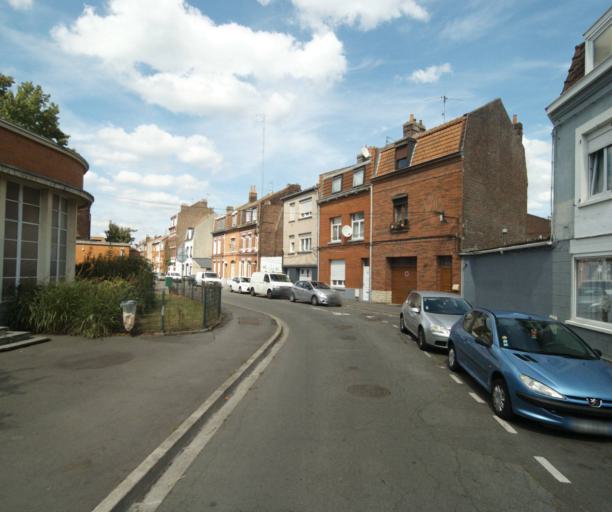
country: FR
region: Nord-Pas-de-Calais
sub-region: Departement du Nord
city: La Madeleine
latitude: 50.6279
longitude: 3.0908
